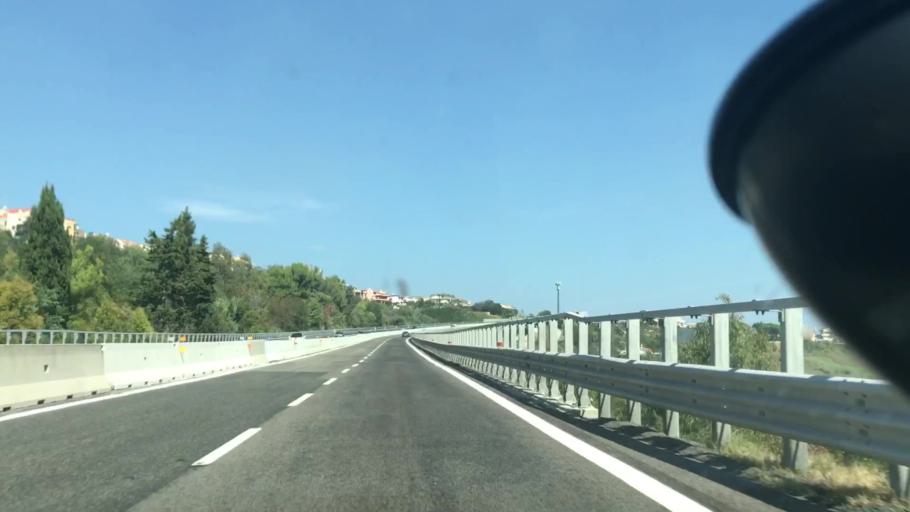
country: IT
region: Abruzzo
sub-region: Provincia di Chieti
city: Marina di Vasto
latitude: 42.0904
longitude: 14.6976
